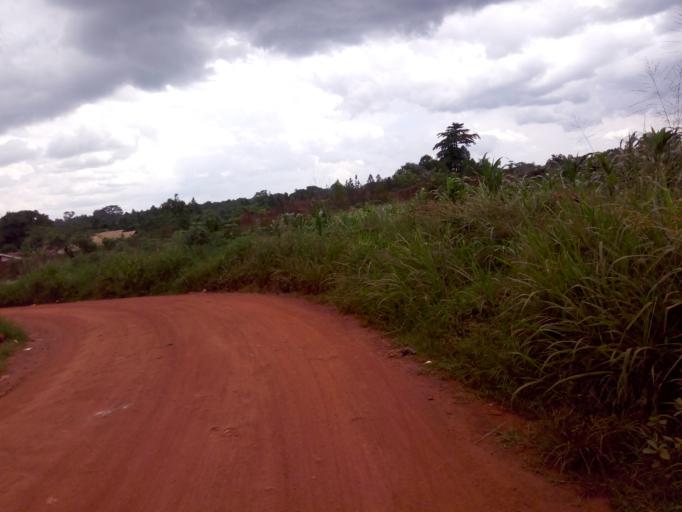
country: UG
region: Western Region
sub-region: Masindi District
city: Masindi
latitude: 1.6824
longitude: 31.7155
